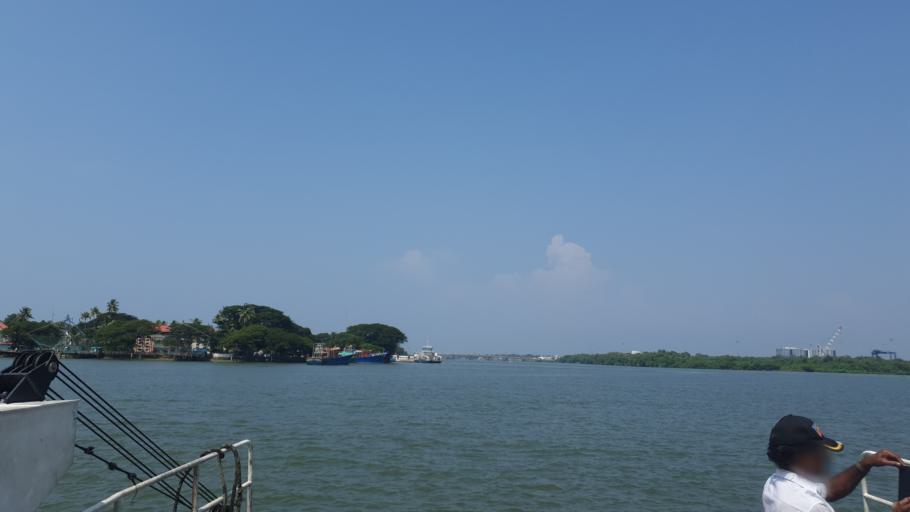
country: IN
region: Kerala
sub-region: Ernakulam
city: Cochin
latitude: 9.9702
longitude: 76.2451
